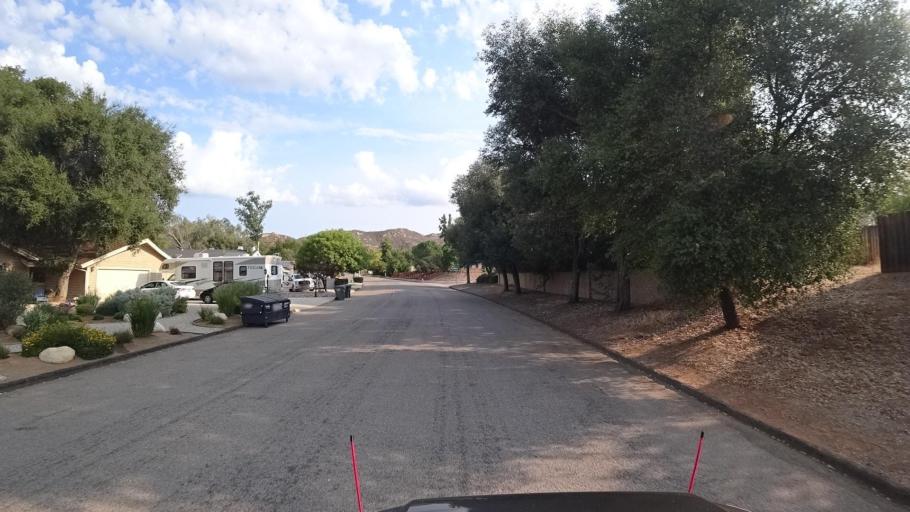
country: US
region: California
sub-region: San Diego County
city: San Diego Country Estates
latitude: 33.0098
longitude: -116.7929
